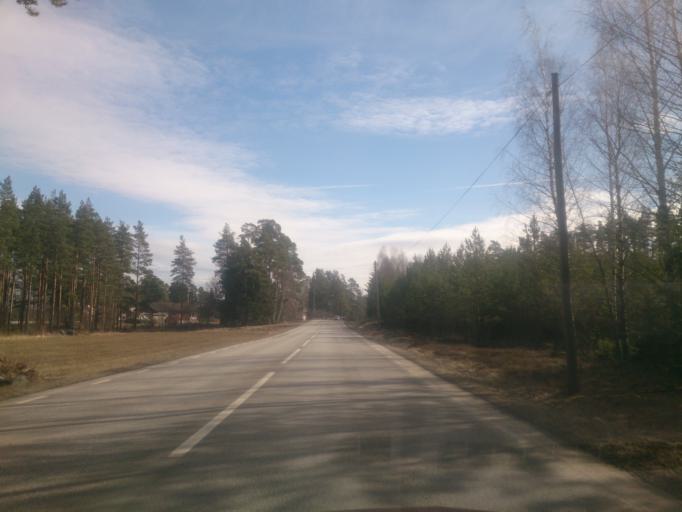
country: SE
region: OEstergoetland
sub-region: Finspangs Kommun
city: Finspang
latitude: 58.6582
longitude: 15.7978
